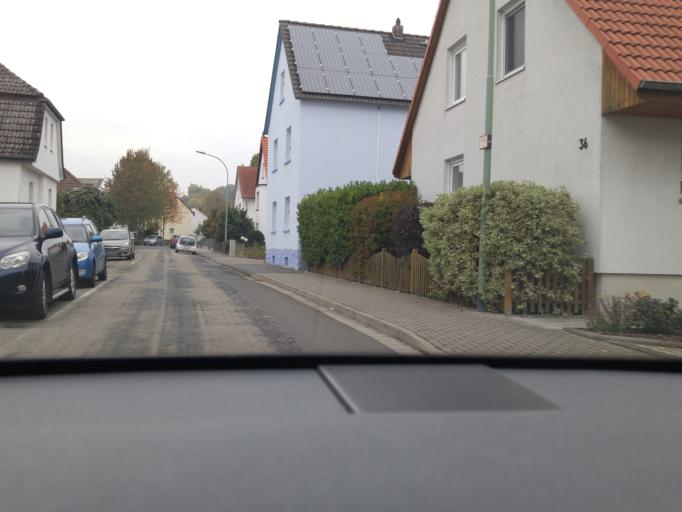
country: DE
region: Hesse
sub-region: Regierungsbezirk Darmstadt
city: Friedberg
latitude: 50.3398
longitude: 8.7627
